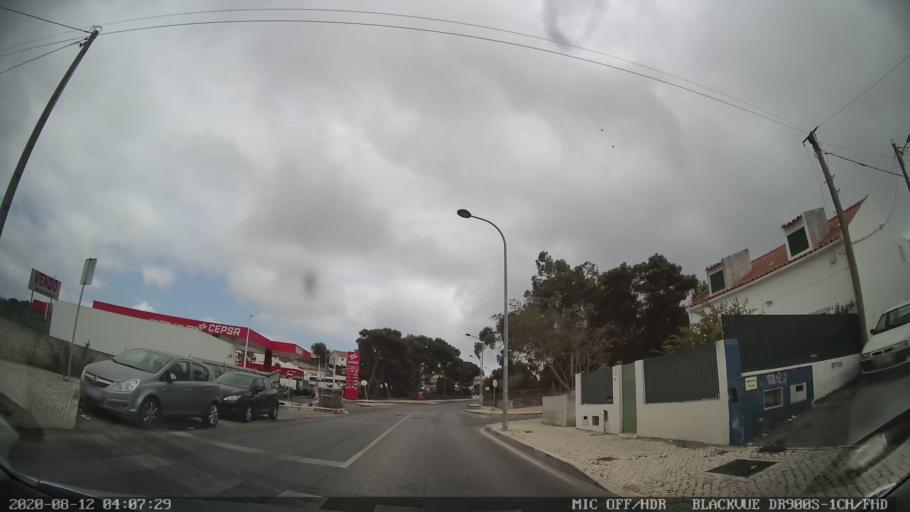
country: PT
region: Lisbon
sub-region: Cascais
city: Estoril
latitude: 38.7117
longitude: -9.3864
